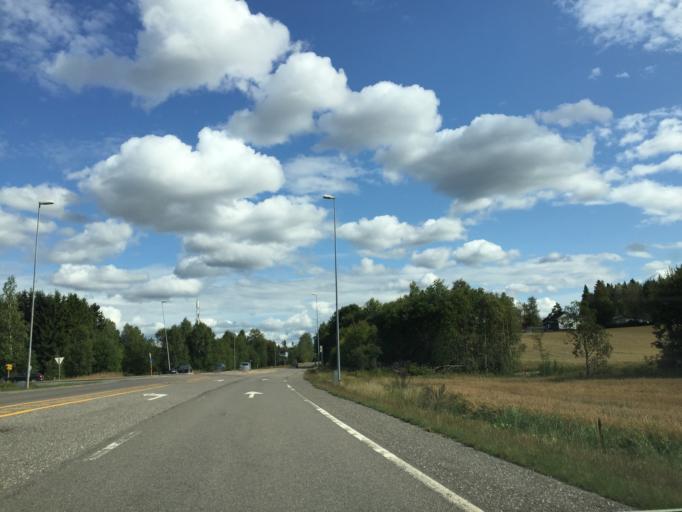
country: NO
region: Ostfold
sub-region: Hobol
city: Knappstad
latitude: 59.6200
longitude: 11.0224
